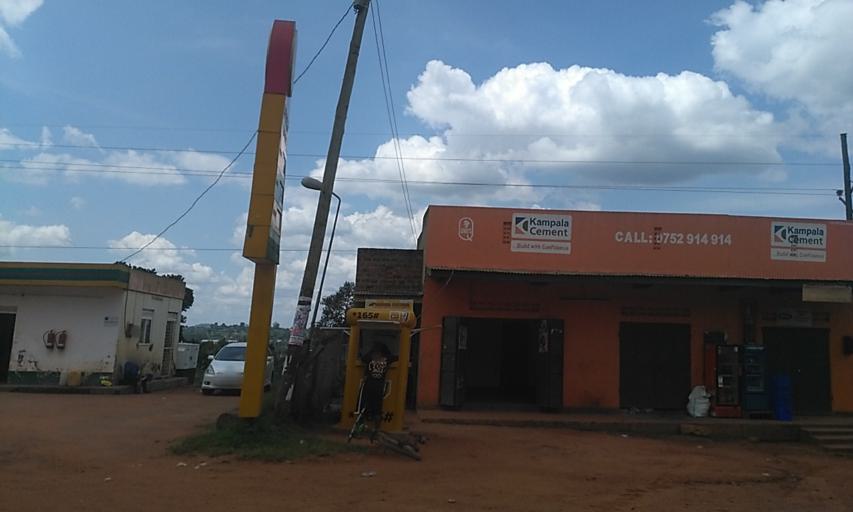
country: UG
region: Central Region
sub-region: Wakiso District
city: Wakiso
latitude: 0.3255
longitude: 32.4597
